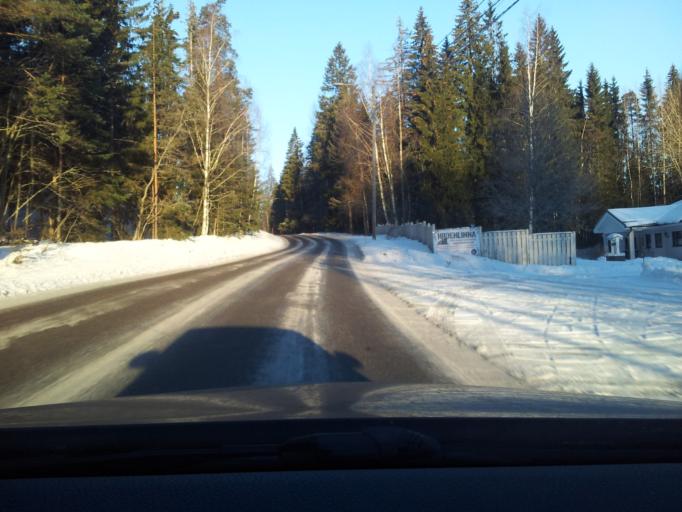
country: FI
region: Uusimaa
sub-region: Helsinki
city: Vihti
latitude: 60.3724
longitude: 24.3715
